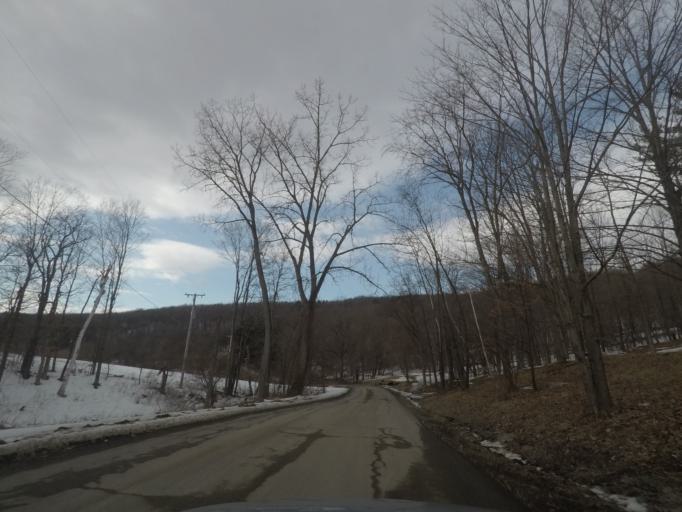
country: US
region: New York
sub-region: Saratoga County
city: Waterford
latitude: 42.7825
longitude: -73.6172
